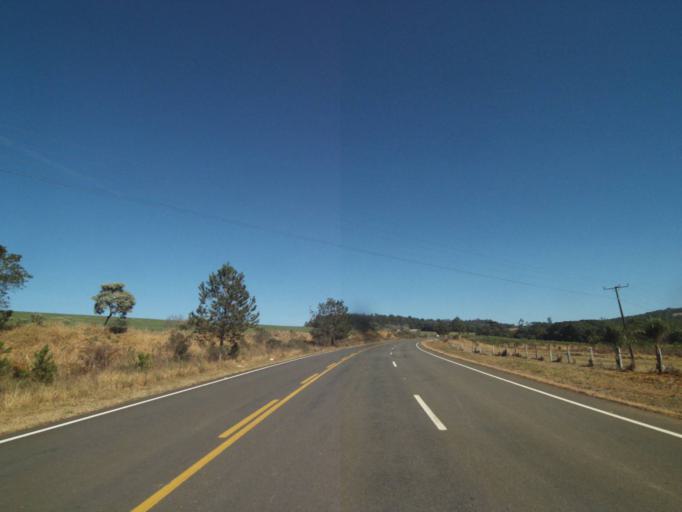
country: BR
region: Parana
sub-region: Tibagi
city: Tibagi
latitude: -24.4682
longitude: -50.4989
